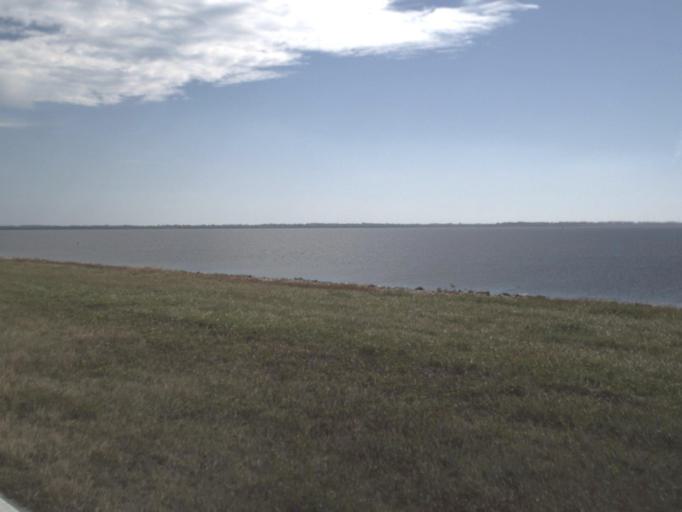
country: US
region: Florida
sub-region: Brevard County
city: Port Saint John
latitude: 28.5270
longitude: -80.7547
